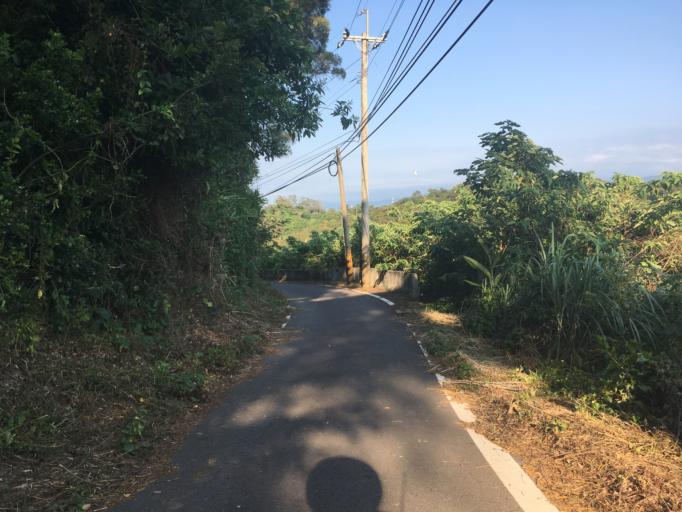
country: TW
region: Taiwan
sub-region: Hsinchu
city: Hsinchu
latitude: 24.7380
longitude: 120.9875
